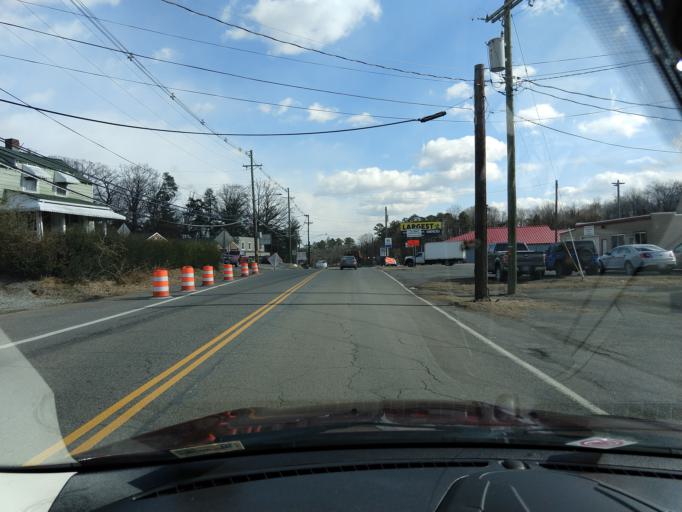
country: US
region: Virginia
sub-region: City of Salem
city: Salem
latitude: 37.2957
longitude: -80.0426
